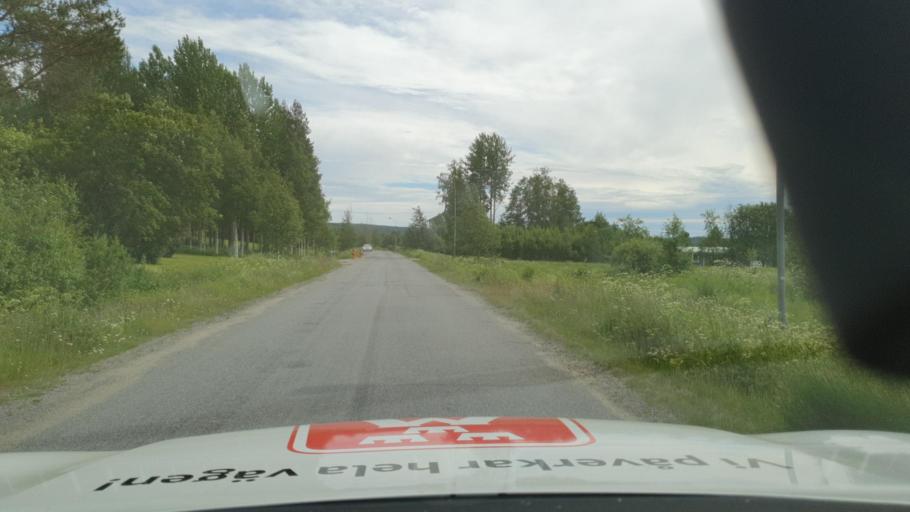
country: SE
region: Vaesterbotten
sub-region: Skelleftea Kommun
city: Burtraesk
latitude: 64.4873
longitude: 20.5058
